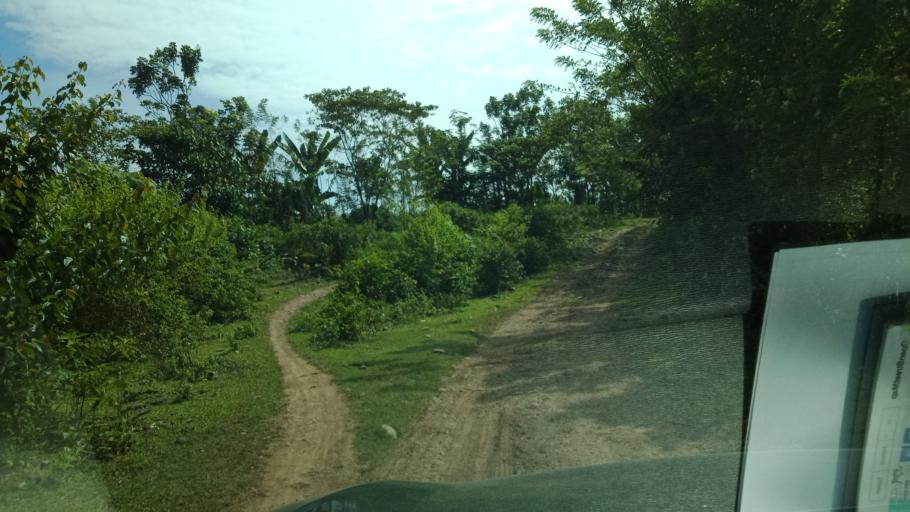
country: ID
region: South Sulawesi
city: Makassar
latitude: -5.2698
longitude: 119.6421
